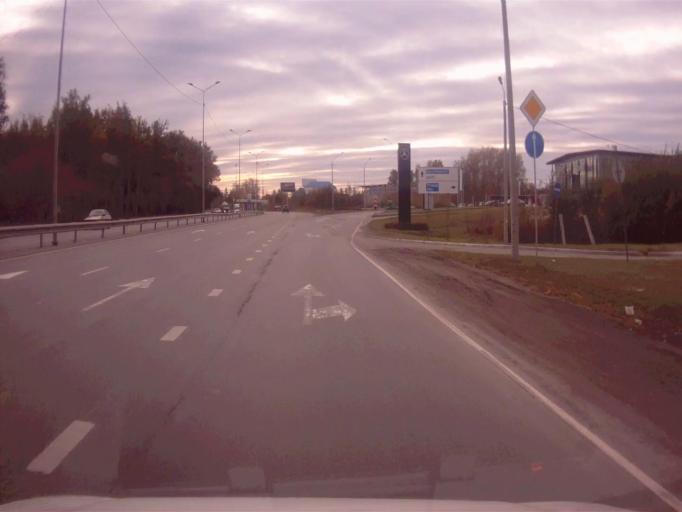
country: RU
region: Chelyabinsk
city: Novosineglazovskiy
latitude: 55.0828
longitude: 61.3934
